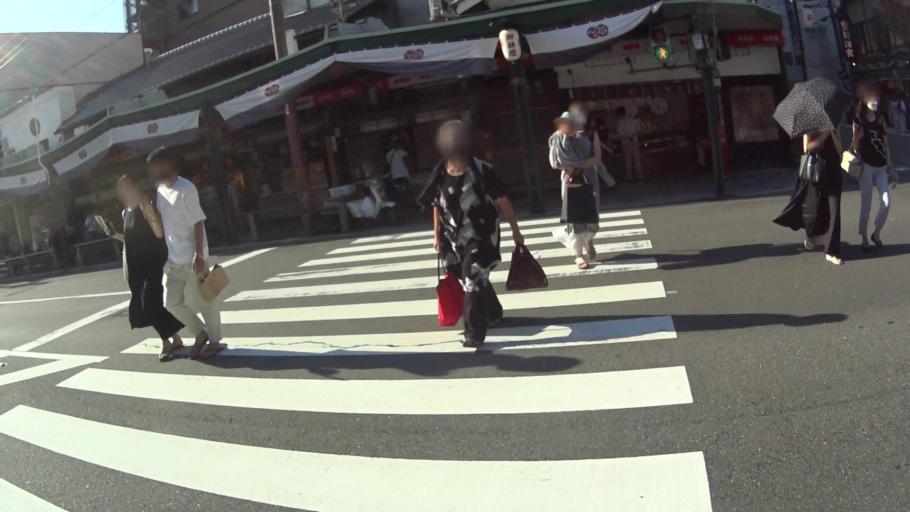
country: RU
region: Rostov
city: Remontnoye
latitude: 46.5031
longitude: 43.7448
